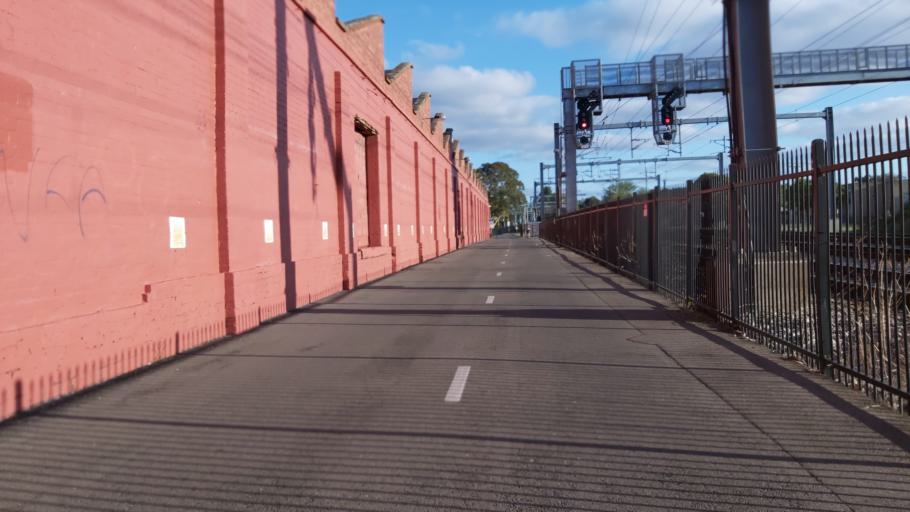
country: AU
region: South Australia
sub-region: Unley
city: Wayville
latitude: -34.9474
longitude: 138.5841
